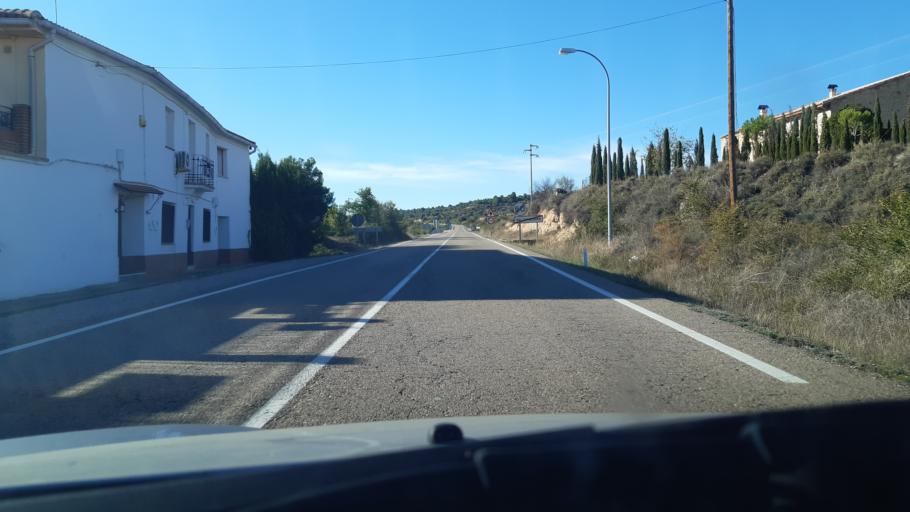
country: ES
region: Aragon
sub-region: Provincia de Teruel
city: Valjunquera
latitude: 40.9522
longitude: 0.0217
